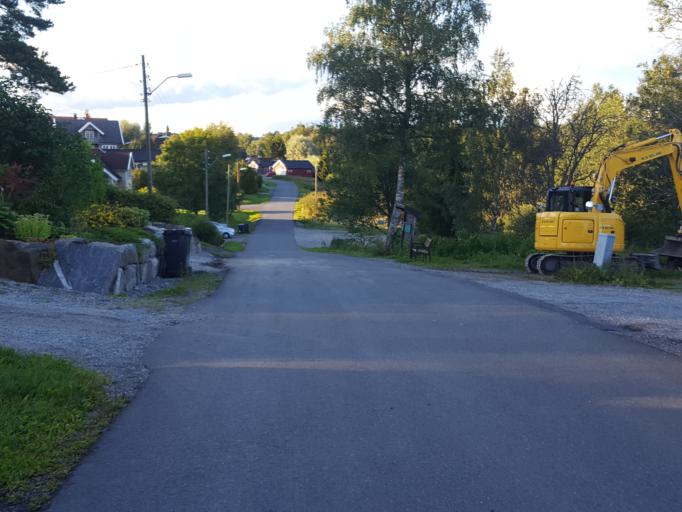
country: NO
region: Akershus
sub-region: Ski
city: Ski
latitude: 59.6792
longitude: 10.8878
